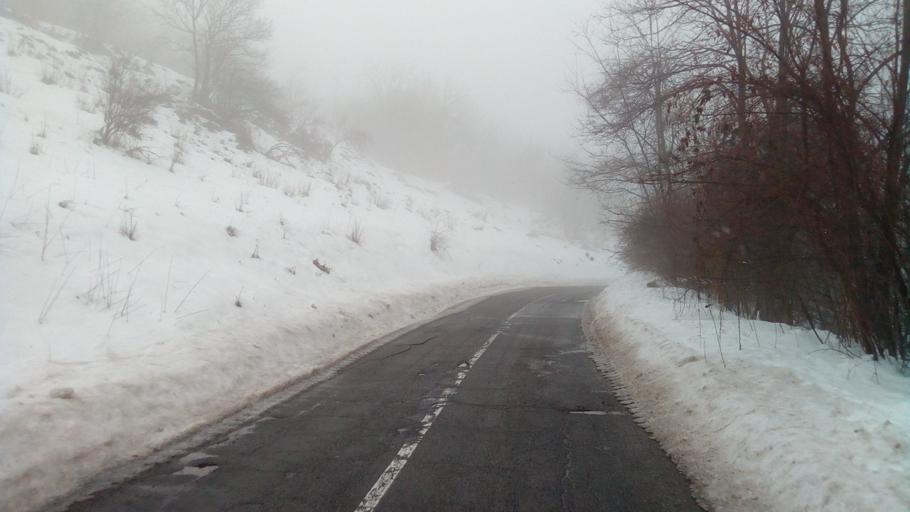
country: HR
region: Sisacko-Moslavacka
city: Petrinja
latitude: 45.3641
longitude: 16.2696
